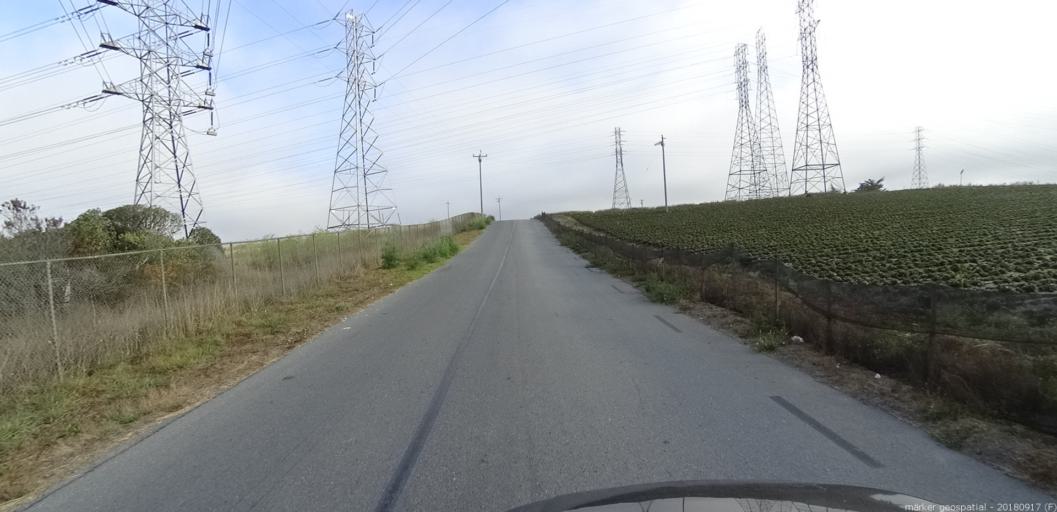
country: US
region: California
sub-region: Monterey County
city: Elkhorn
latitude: 36.7998
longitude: -121.7538
